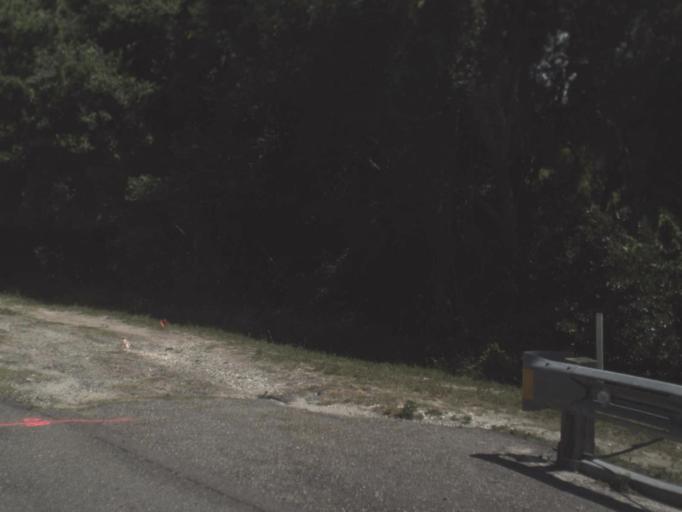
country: US
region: Florida
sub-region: Duval County
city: Atlantic Beach
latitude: 30.3927
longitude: -81.4588
